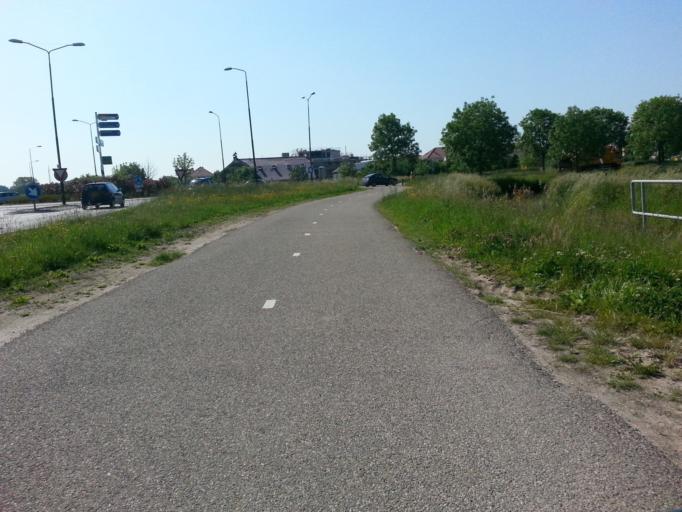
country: NL
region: Utrecht
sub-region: Gemeente Wijk bij Duurstede
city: Wijk bij Duurstede
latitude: 51.9872
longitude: 5.3319
